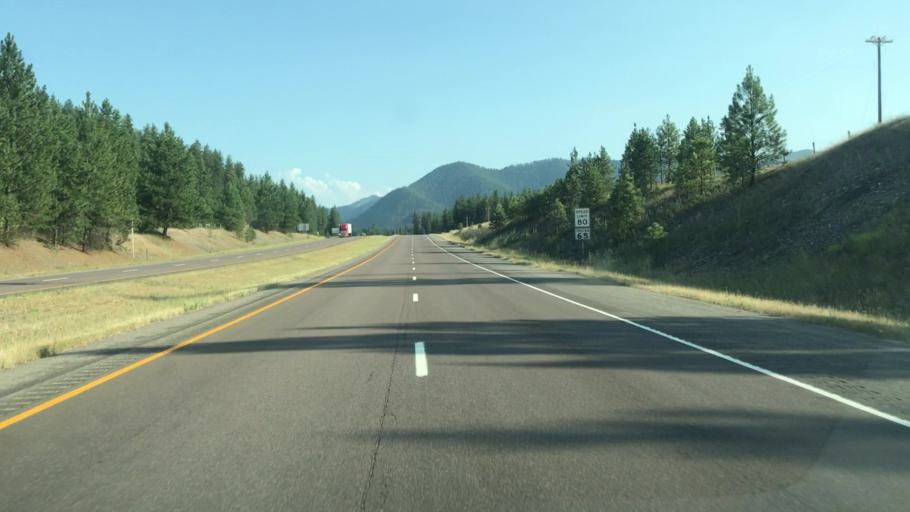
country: US
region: Montana
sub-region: Mineral County
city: Superior
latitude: 47.0658
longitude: -114.7643
